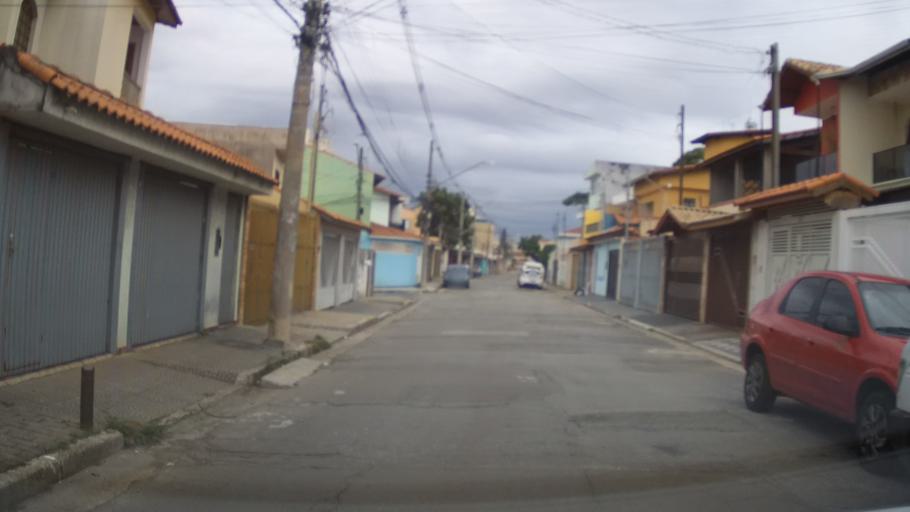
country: BR
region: Sao Paulo
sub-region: Guarulhos
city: Guarulhos
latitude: -23.4556
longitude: -46.5565
